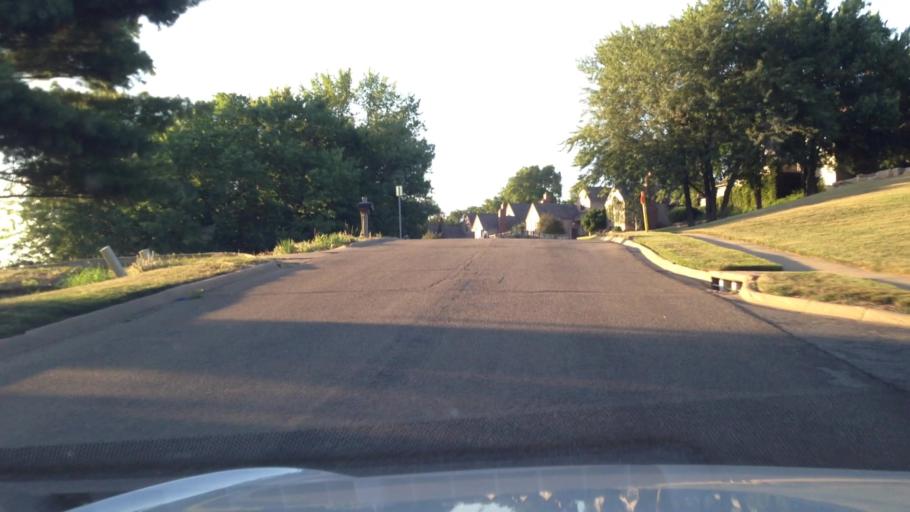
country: US
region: Kansas
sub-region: Douglas County
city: Lawrence
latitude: 38.9471
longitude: -95.2900
